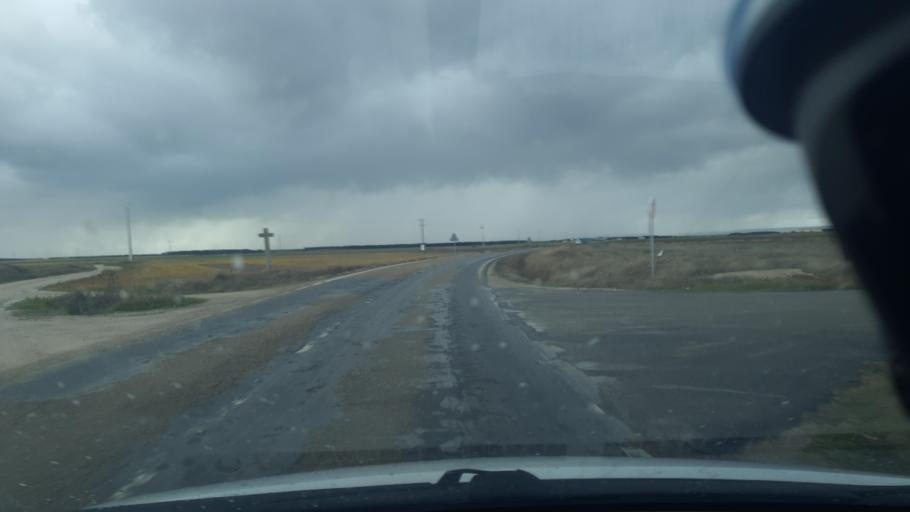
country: ES
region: Castille and Leon
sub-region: Provincia de Segovia
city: Chane
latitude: 41.3115
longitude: -4.3693
